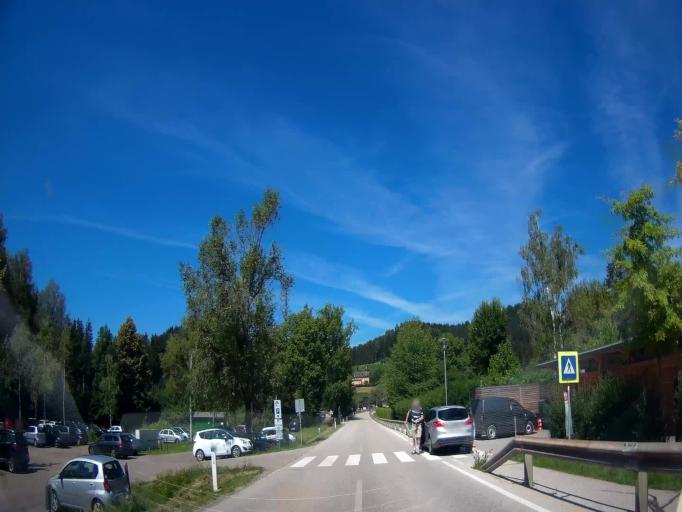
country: AT
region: Carinthia
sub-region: Politischer Bezirk Sankt Veit an der Glan
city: St. Georgen am Laengsee
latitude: 46.7833
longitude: 14.4238
